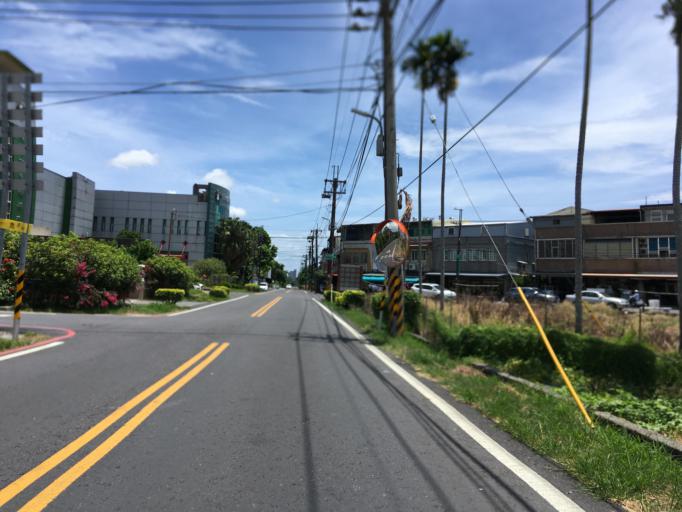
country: TW
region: Taiwan
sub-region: Yilan
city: Yilan
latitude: 24.6595
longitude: 121.7346
